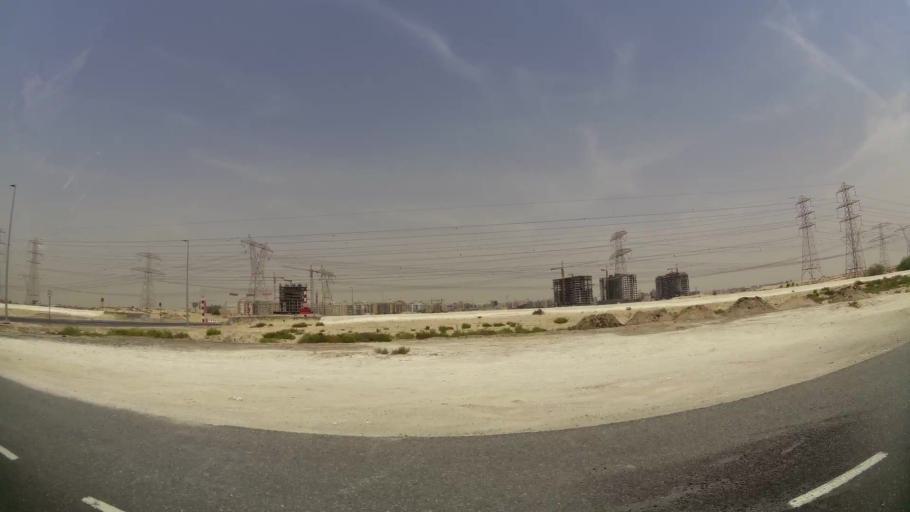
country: AE
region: Ash Shariqah
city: Sharjah
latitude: 25.1946
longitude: 55.3900
